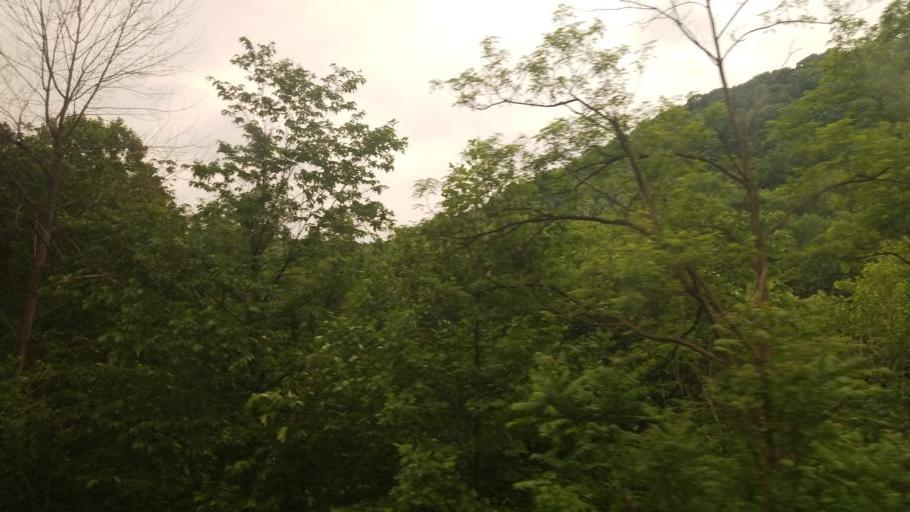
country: US
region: Pennsylvania
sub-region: Fayette County
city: South Connellsville
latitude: 39.9271
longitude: -79.4835
